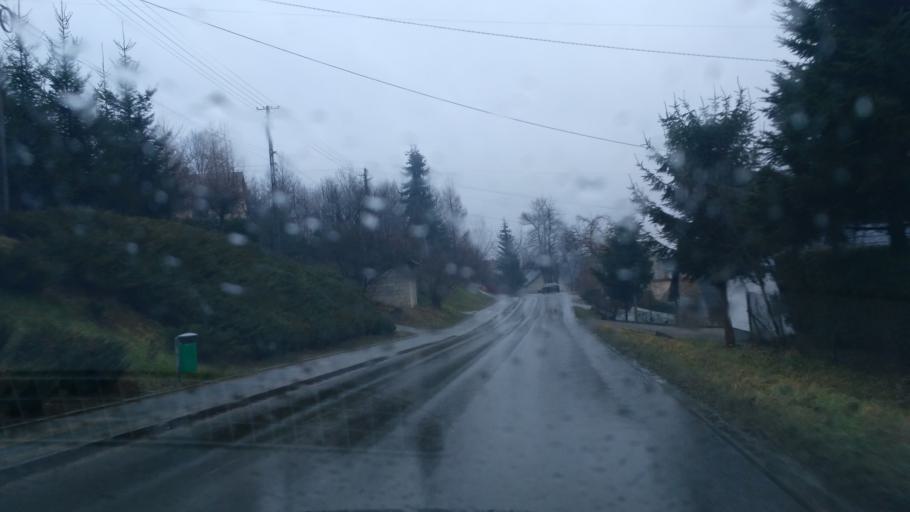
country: PL
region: Subcarpathian Voivodeship
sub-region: Powiat krosnienski
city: Kroscienko Wyzne
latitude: 49.6795
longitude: 21.8272
